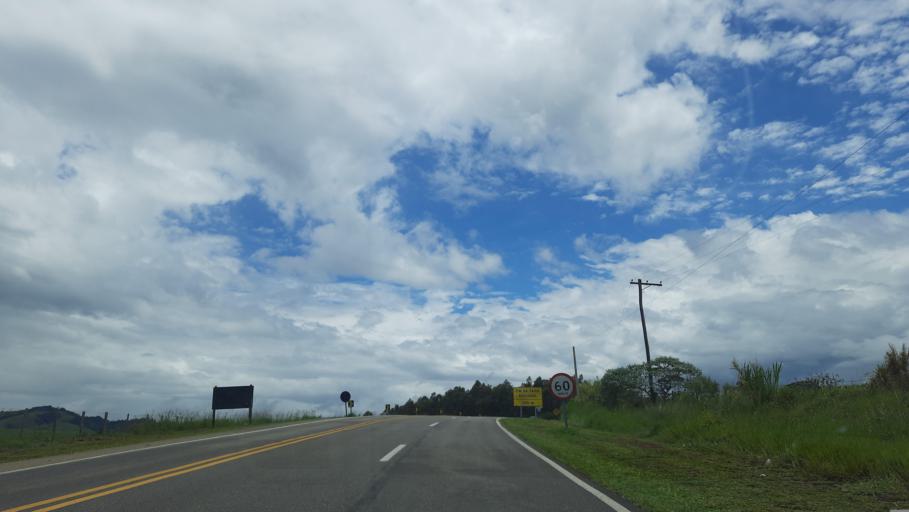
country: BR
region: Sao Paulo
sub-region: Vargem Grande Do Sul
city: Vargem Grande do Sul
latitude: -21.8020
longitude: -46.7986
